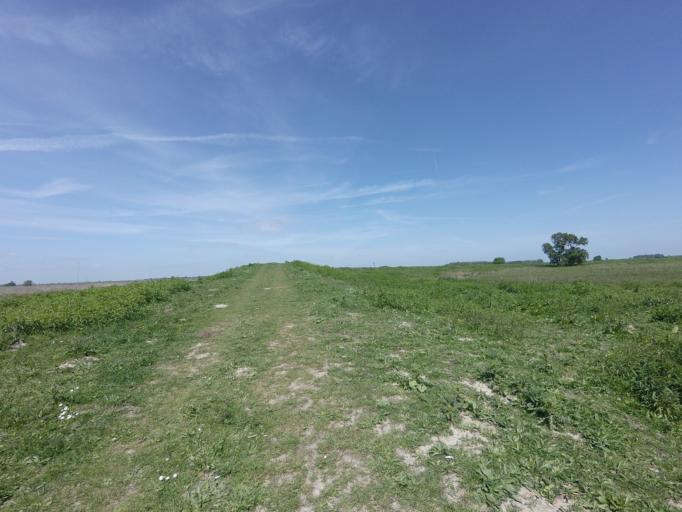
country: NL
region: South Holland
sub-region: Gemeente Spijkenisse
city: Spijkenisse
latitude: 51.7509
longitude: 4.2772
